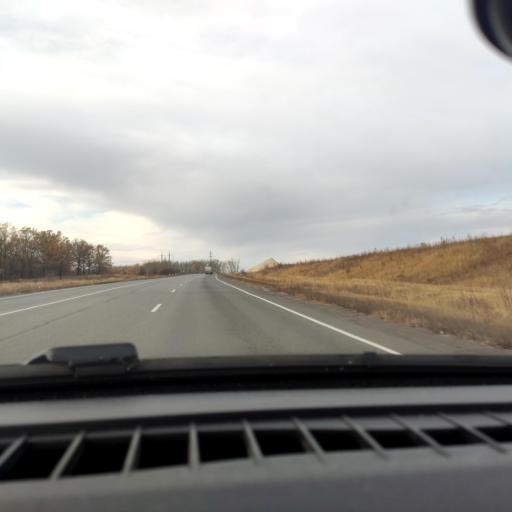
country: RU
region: Voronezj
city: Ostrogozhsk
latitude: 50.9411
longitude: 39.0553
